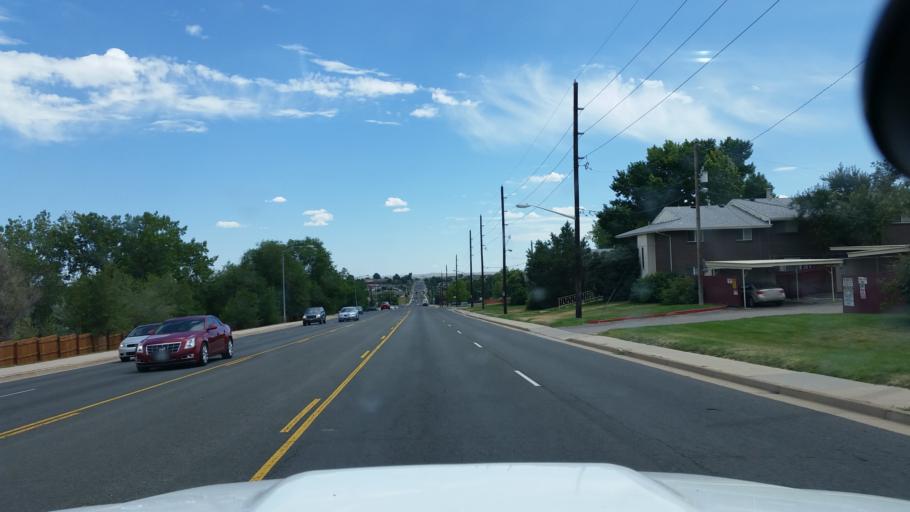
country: US
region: Colorado
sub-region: Adams County
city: Federal Heights
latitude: 39.8562
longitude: -105.0007
